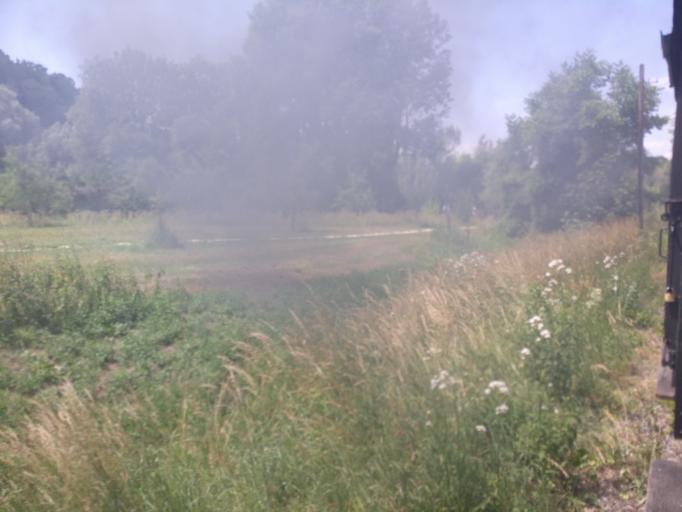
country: AT
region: Upper Austria
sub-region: Politischer Bezirk Steyr-Land
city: Garsten
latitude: 48.0406
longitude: 14.3850
